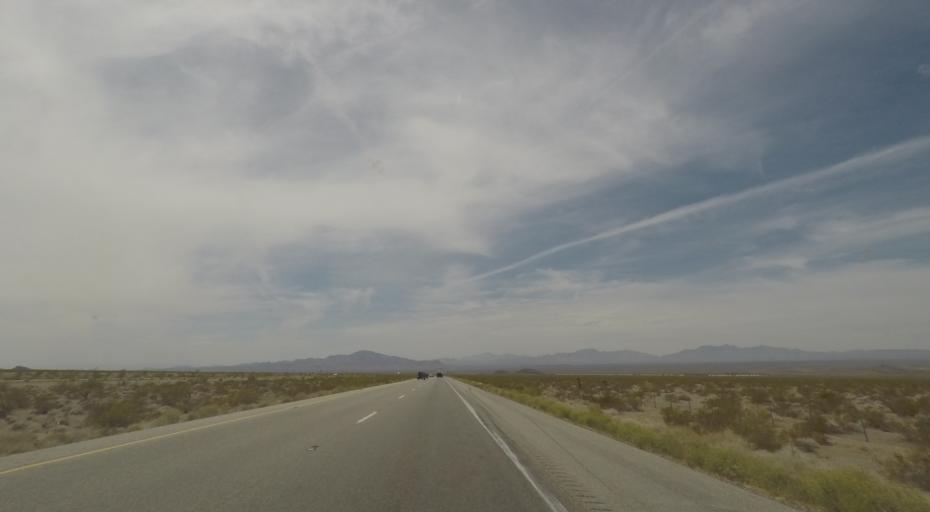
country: US
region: California
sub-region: San Bernardino County
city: Needles
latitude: 34.8213
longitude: -115.1203
